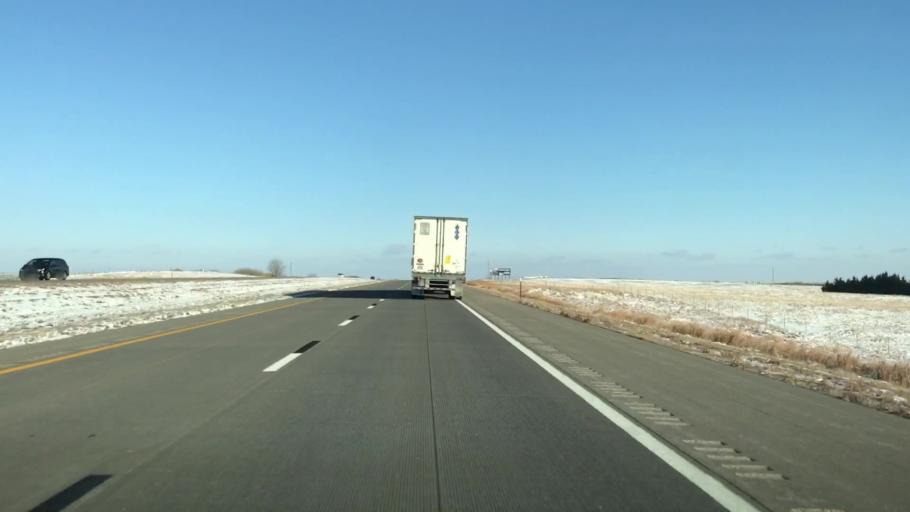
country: US
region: Kansas
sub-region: Lincoln County
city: Lincoln
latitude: 38.8782
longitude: -97.9891
